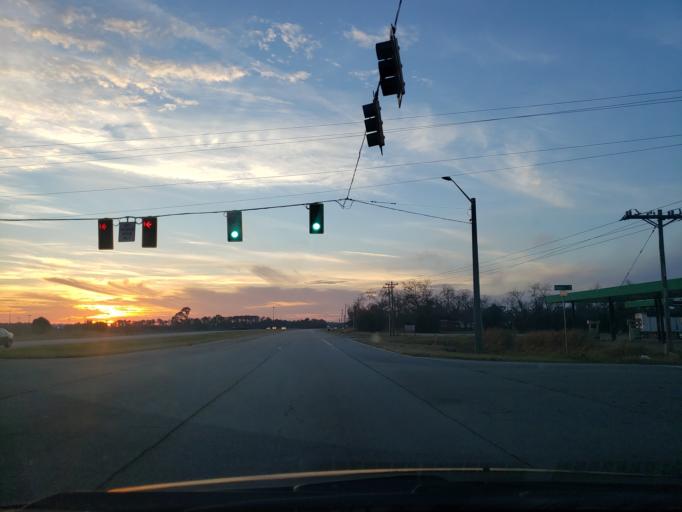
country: US
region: Georgia
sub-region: Dougherty County
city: Albany
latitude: 31.5726
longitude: -84.0515
